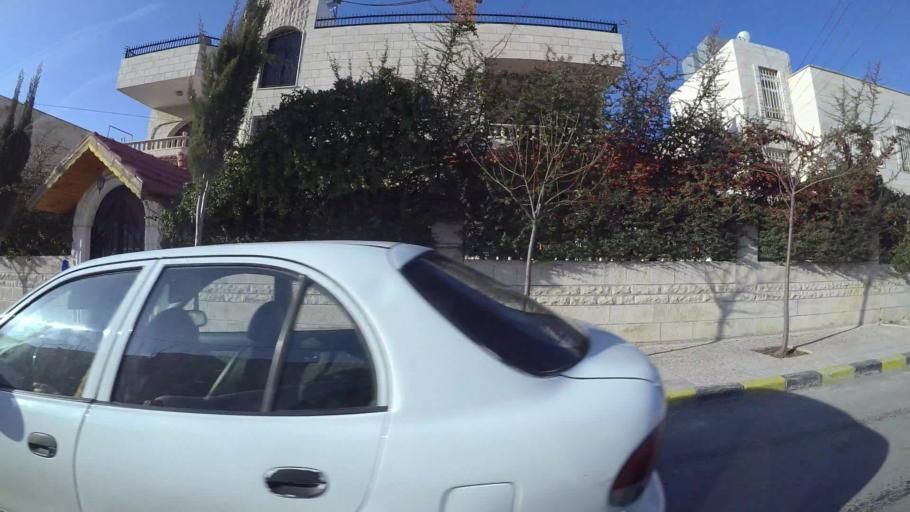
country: JO
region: Amman
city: Al Bunayyat ash Shamaliyah
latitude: 31.9023
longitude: 35.9109
